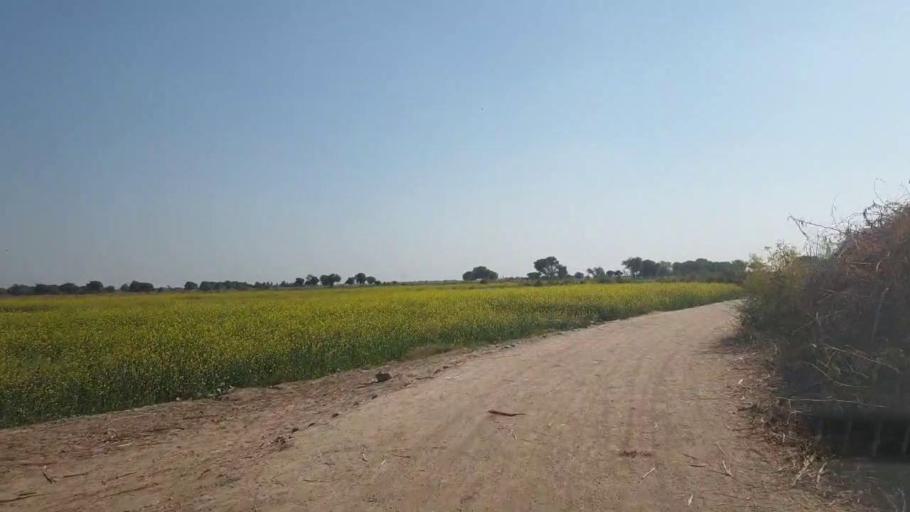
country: PK
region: Sindh
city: Chambar
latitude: 25.3103
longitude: 68.7207
